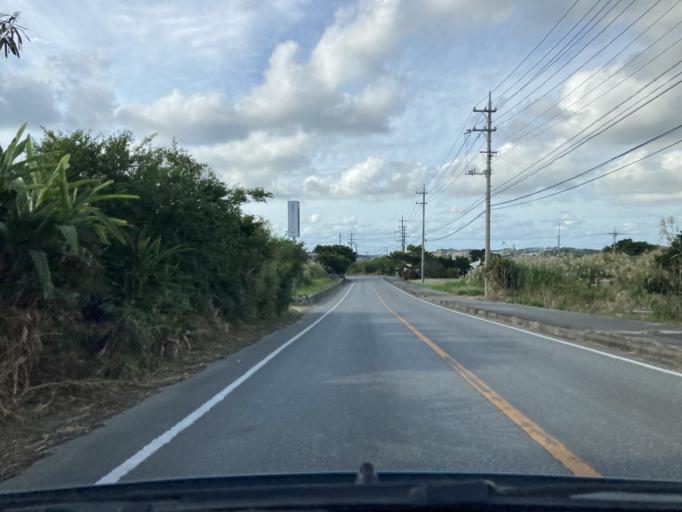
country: JP
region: Okinawa
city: Itoman
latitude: 26.1302
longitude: 127.7120
